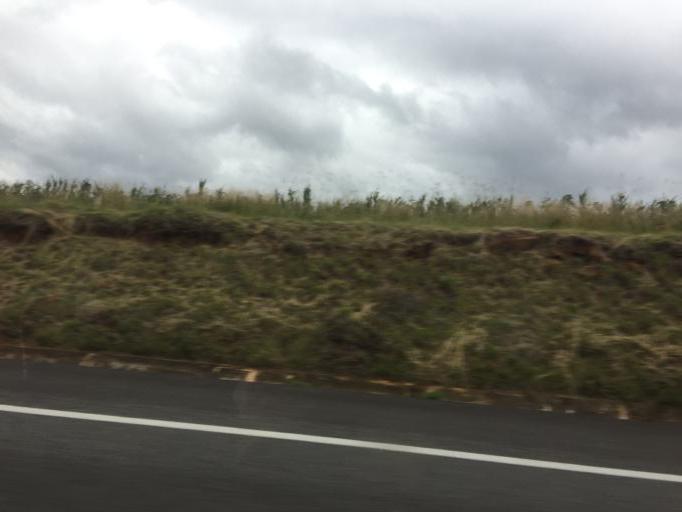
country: MX
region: Jalisco
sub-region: Zapotlanejo
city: La Mezquitera
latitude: 20.5496
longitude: -103.0399
